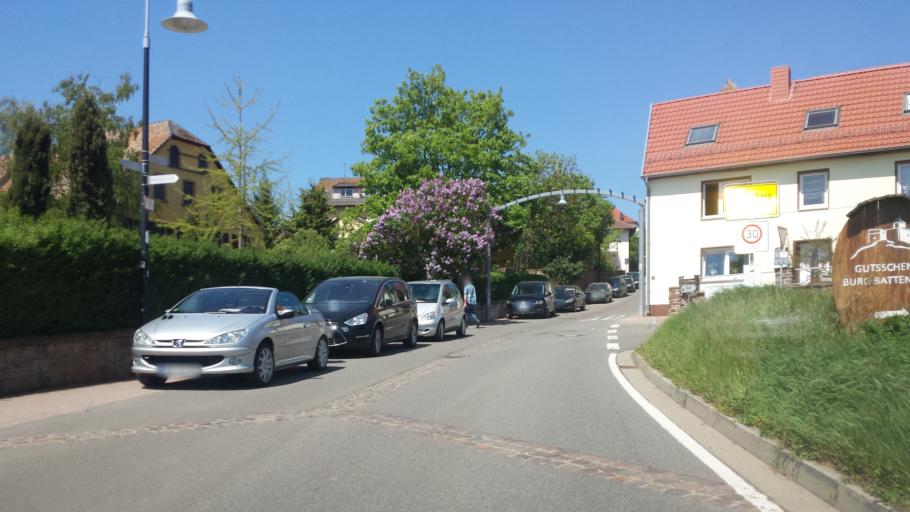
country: DE
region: Rheinland-Pfalz
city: Neuleiningen
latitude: 49.5320
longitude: 8.1419
